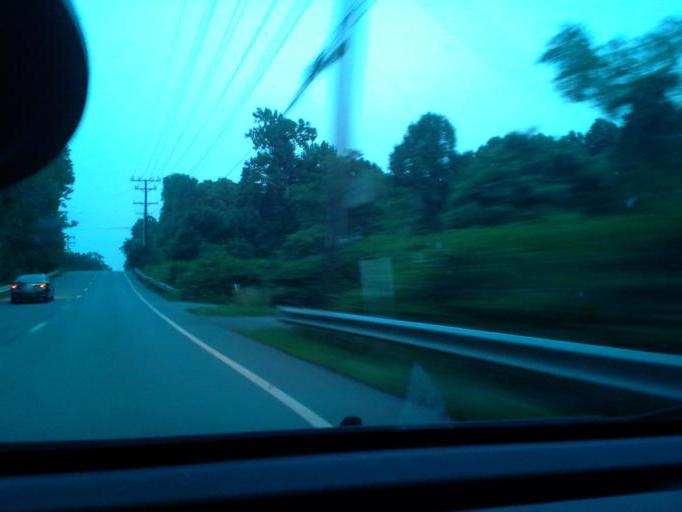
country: US
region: Maryland
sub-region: Calvert County
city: Chesapeake Beach
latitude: 38.7026
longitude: -76.5672
